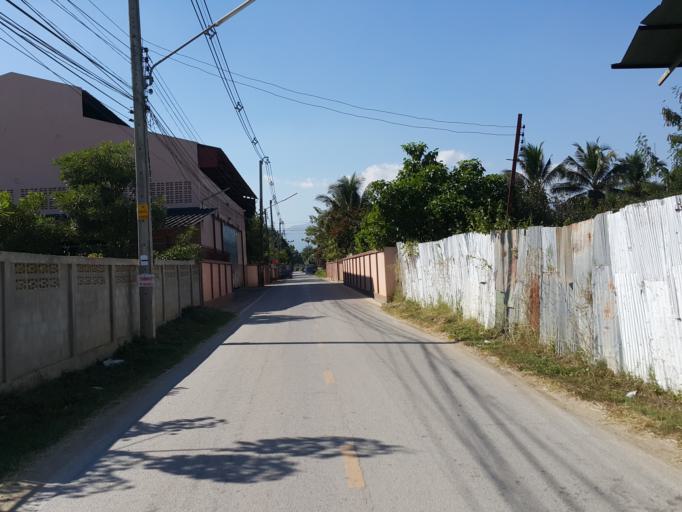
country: TH
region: Chiang Mai
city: Chiang Mai
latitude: 18.7737
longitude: 99.0332
